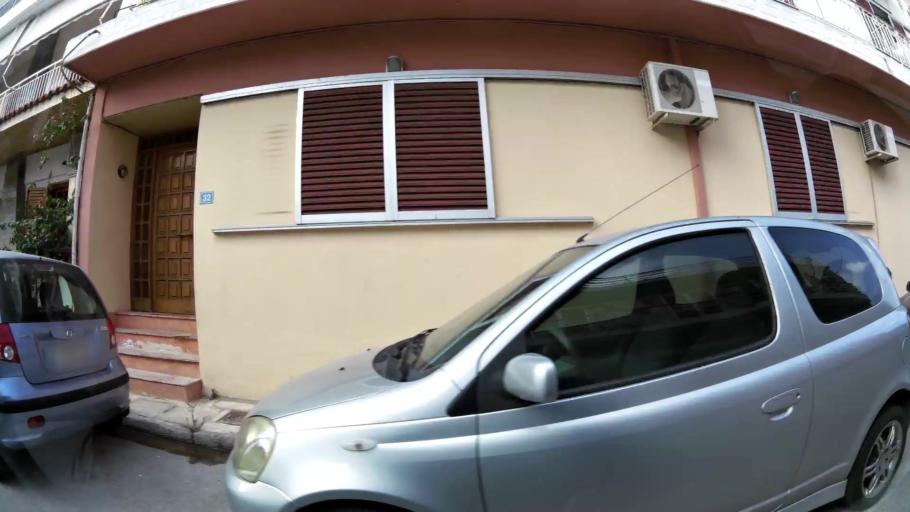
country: GR
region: Attica
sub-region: Nomarchia Athinas
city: Ilion
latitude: 38.0436
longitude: 23.7035
